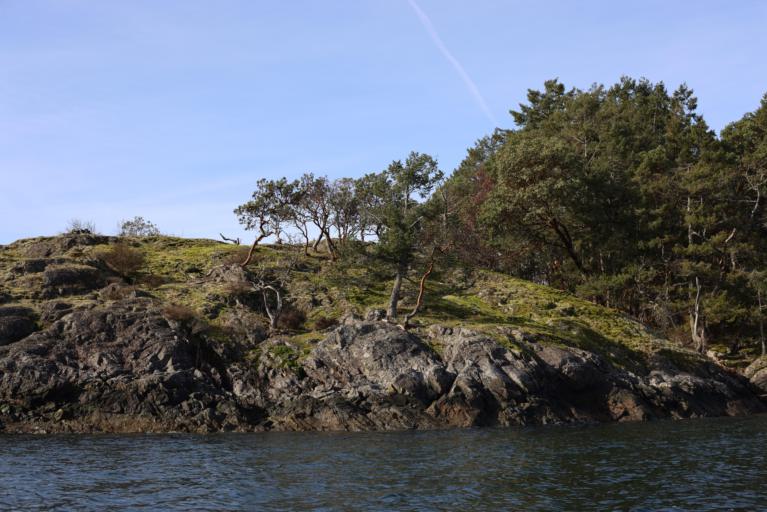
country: CA
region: British Columbia
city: Duncan
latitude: 48.7435
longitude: -123.5692
